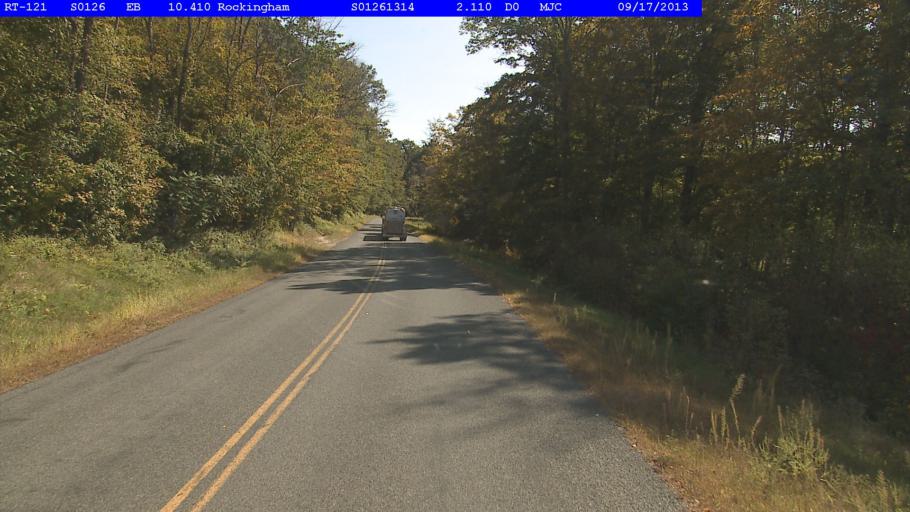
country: US
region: Vermont
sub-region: Windham County
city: Rockingham
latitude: 43.1359
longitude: -72.5233
